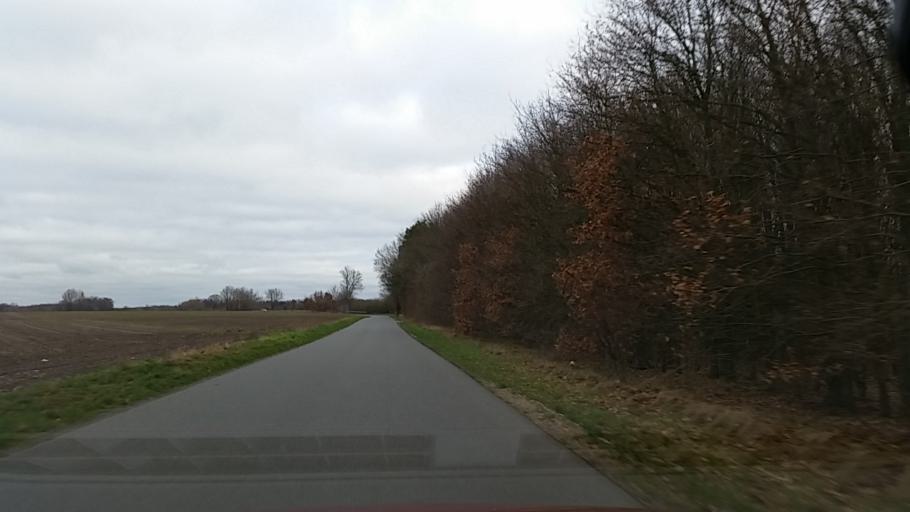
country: DE
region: Lower Saxony
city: Luder
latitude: 52.8187
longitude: 10.6695
